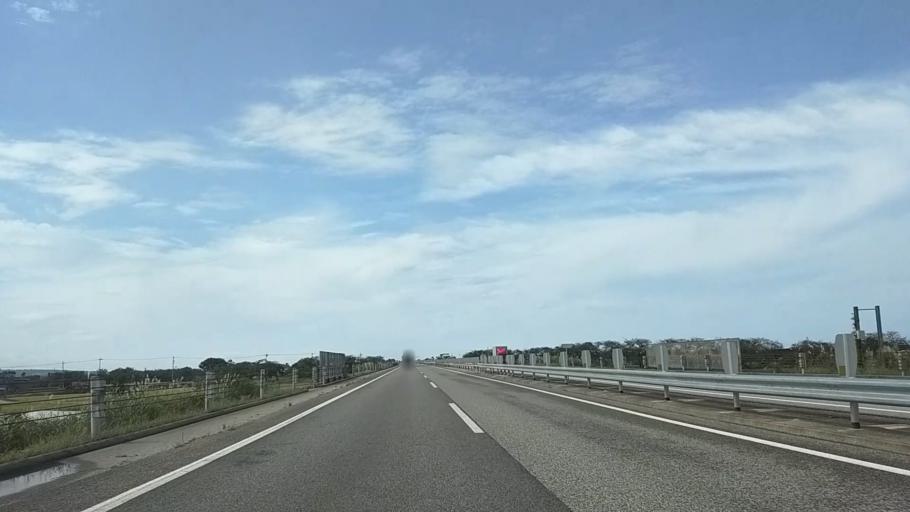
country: JP
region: Toyama
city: Nyuzen
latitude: 36.9359
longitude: 137.5424
